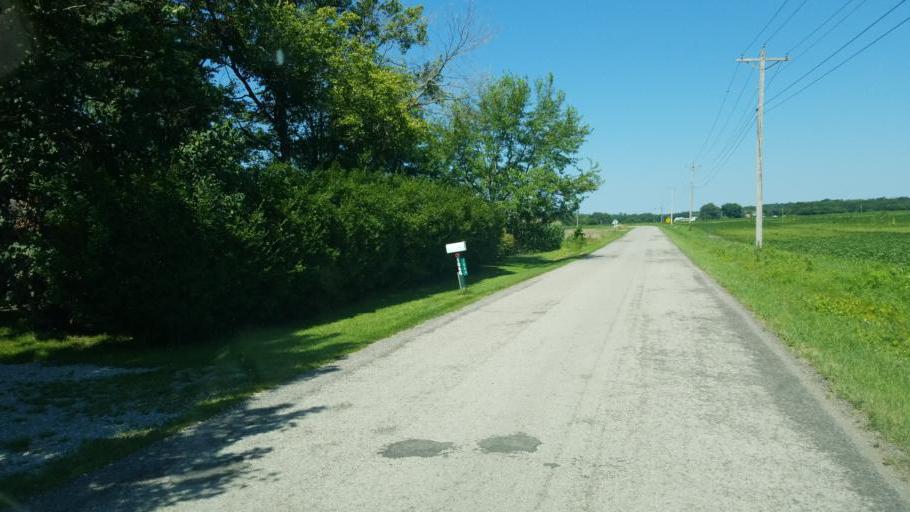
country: US
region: Ohio
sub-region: Delaware County
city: Ashley
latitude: 40.4308
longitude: -82.9690
